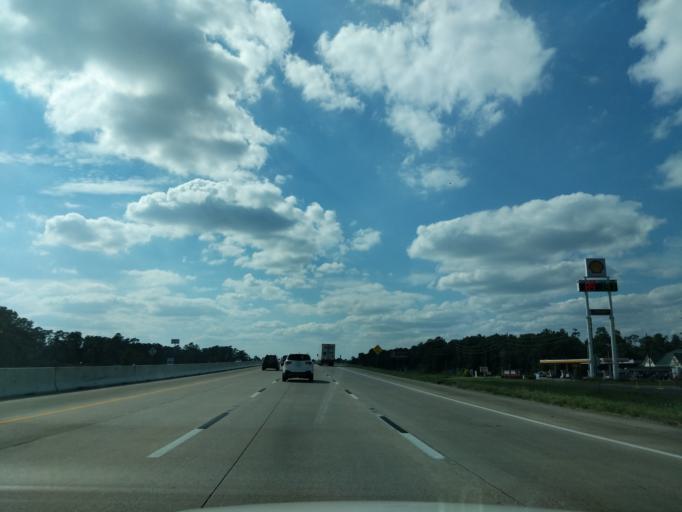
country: US
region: Texas
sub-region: Chambers County
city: Anahuac
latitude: 29.8405
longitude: -94.6458
